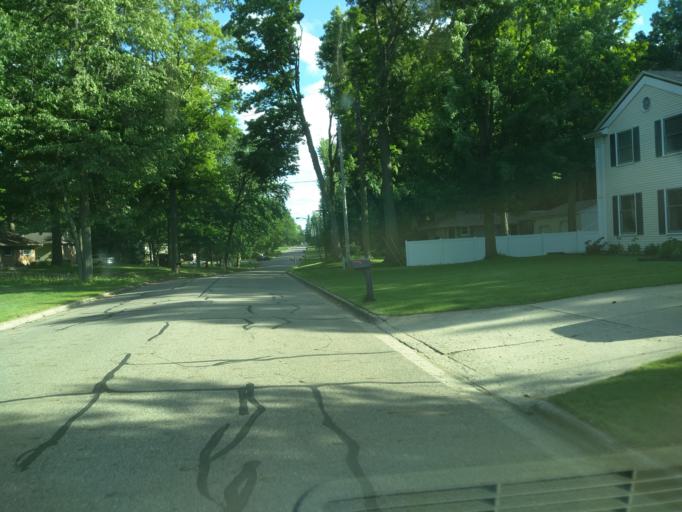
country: US
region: Michigan
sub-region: Eaton County
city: Waverly
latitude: 42.7486
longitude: -84.6169
